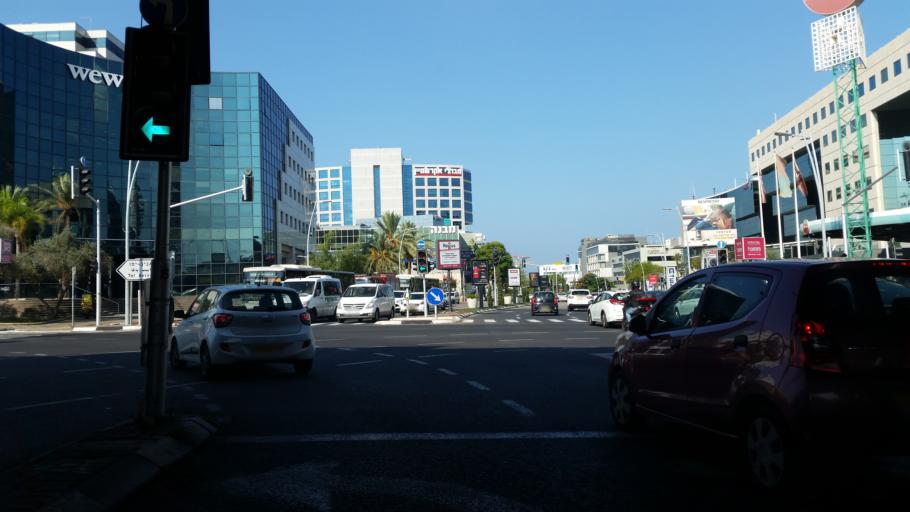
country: IL
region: Tel Aviv
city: Herzliyya
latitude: 32.1606
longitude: 34.8112
